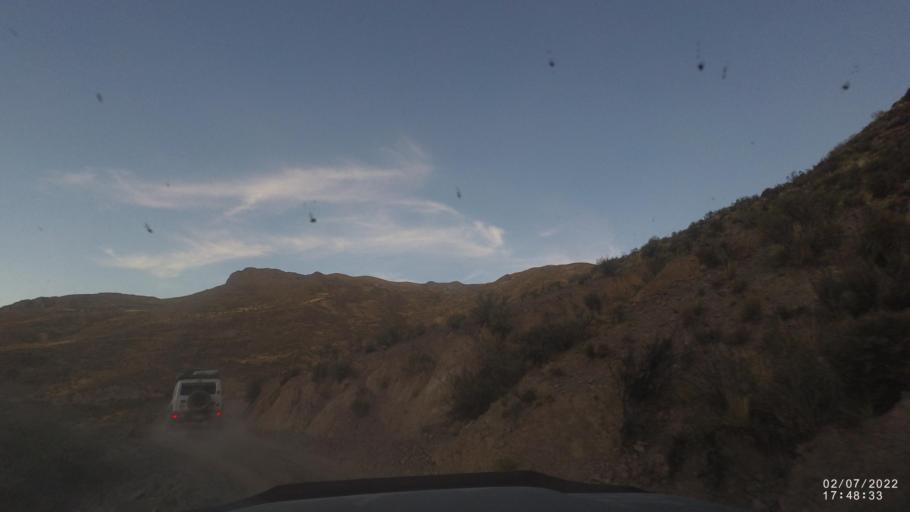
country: BO
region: Cochabamba
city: Irpa Irpa
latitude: -17.8517
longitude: -66.6197
